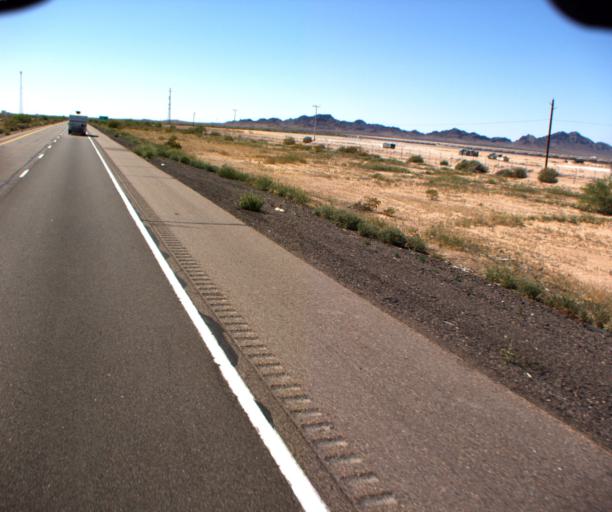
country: US
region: Arizona
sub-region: Maricopa County
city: Gila Bend
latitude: 32.9096
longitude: -112.9720
